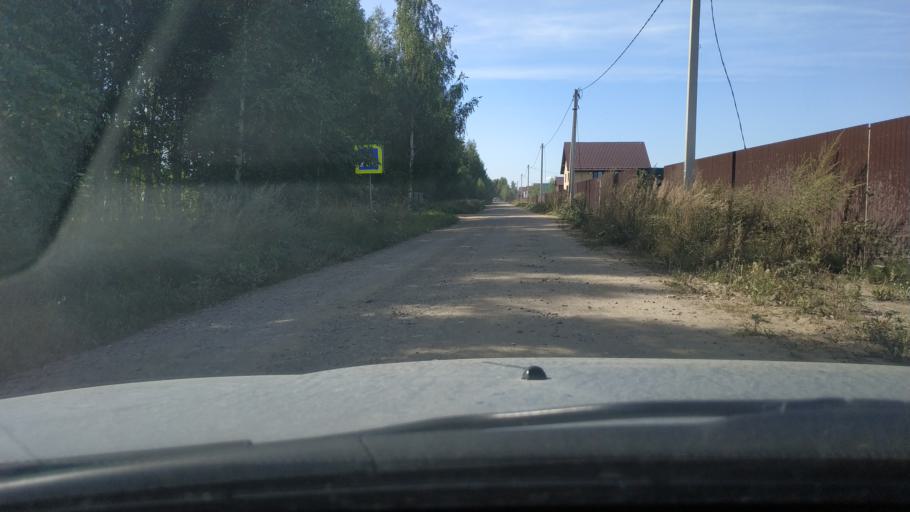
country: RU
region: Kostroma
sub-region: Kostromskoy Rayon
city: Kostroma
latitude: 57.7782
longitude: 40.7448
